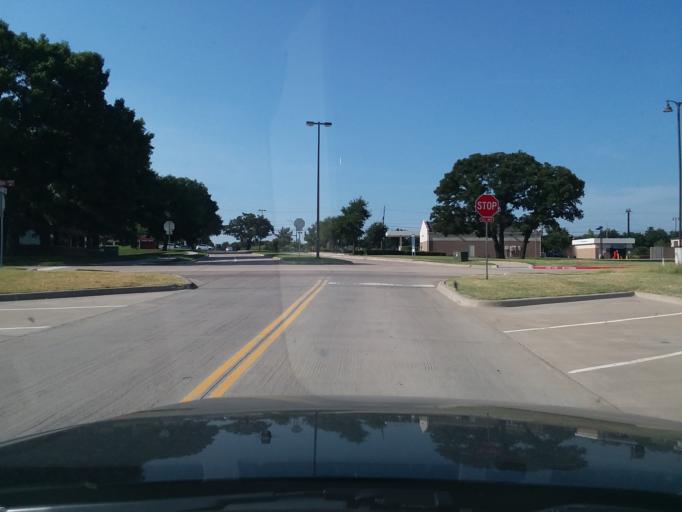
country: US
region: Texas
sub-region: Denton County
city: Flower Mound
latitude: 33.0366
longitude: -97.0655
